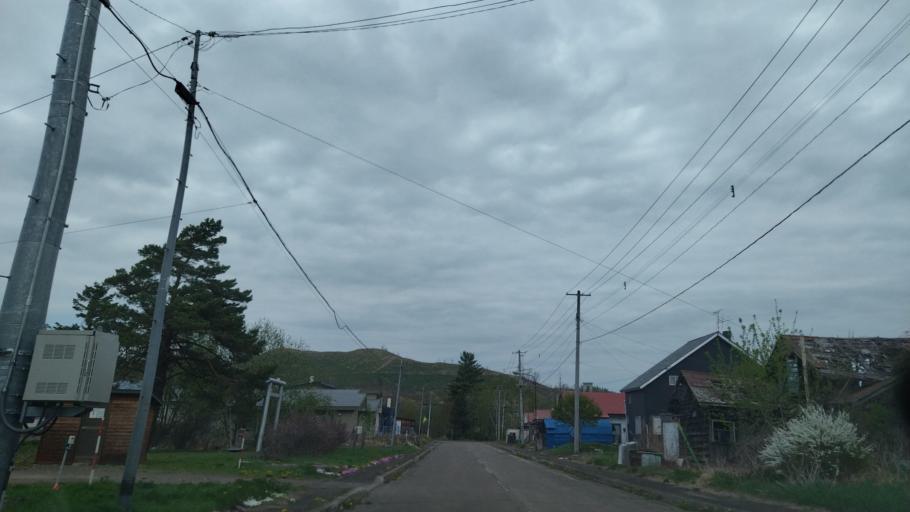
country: JP
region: Hokkaido
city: Kitami
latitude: 43.3530
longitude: 143.6046
